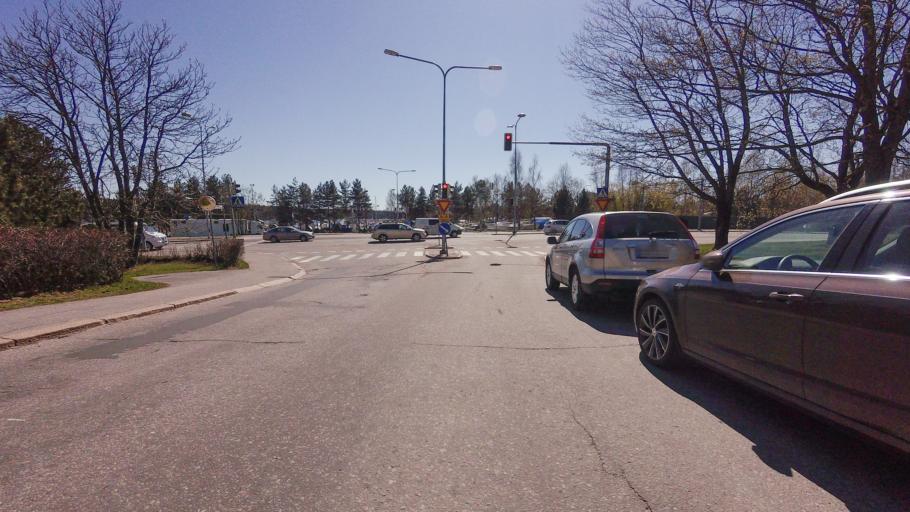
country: FI
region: Uusimaa
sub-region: Helsinki
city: Vantaa
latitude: 60.2082
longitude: 25.1000
